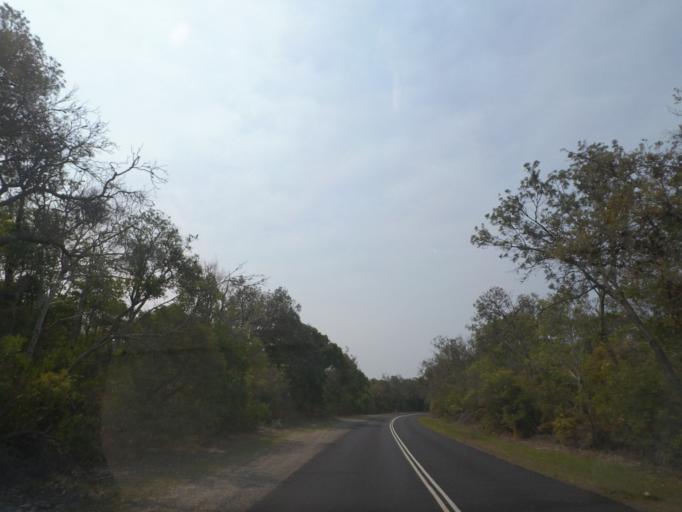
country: AU
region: New South Wales
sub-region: Tweed
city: Pottsville Beach
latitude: -28.4430
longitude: 153.5546
